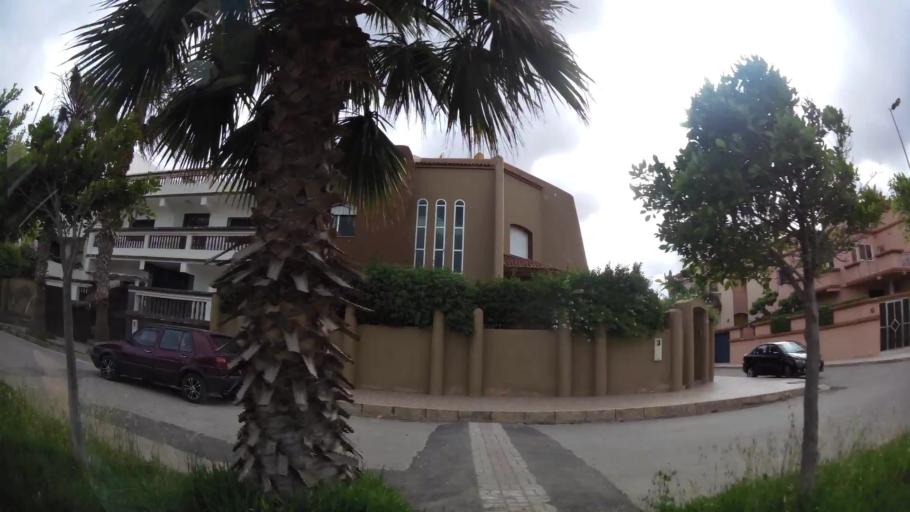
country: MA
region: Oriental
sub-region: Nador
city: Nador
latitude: 35.1657
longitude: -2.9141
